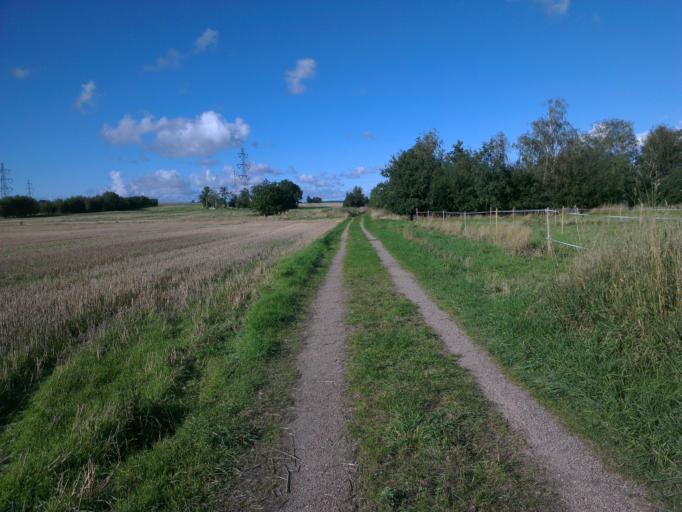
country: DK
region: Capital Region
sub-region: Frederikssund Kommune
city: Frederikssund
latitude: 55.7924
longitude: 12.0423
